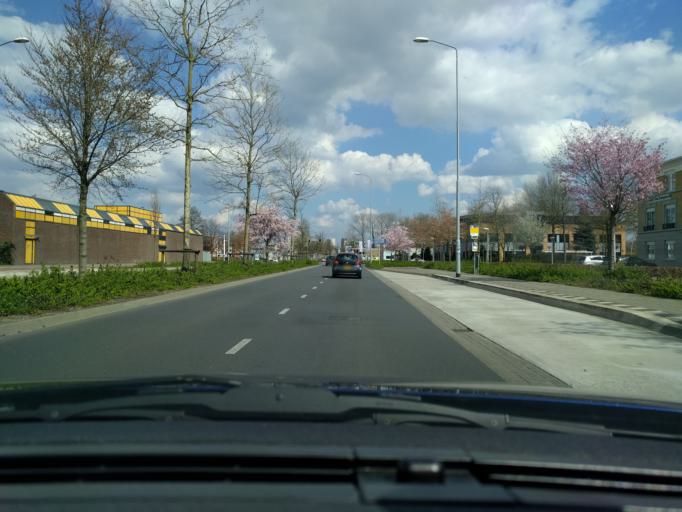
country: NL
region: North Brabant
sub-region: Gemeente Eindhoven
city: Eindhoven
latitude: 51.4281
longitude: 5.4457
